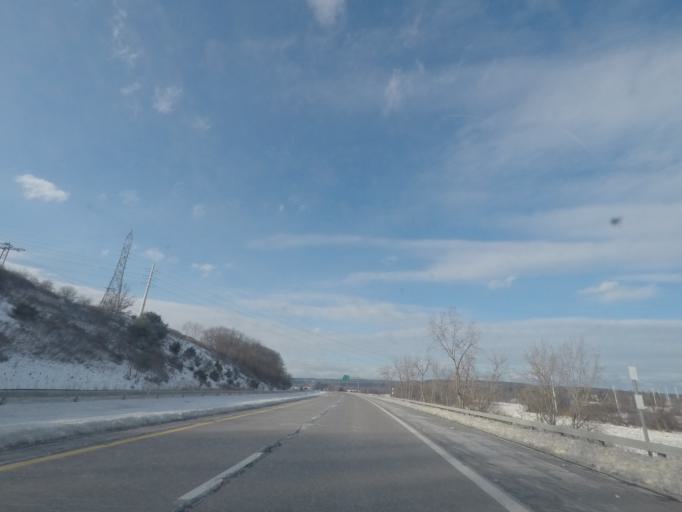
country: US
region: New York
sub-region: Schenectady County
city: Scotia
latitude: 42.8310
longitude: -73.9940
